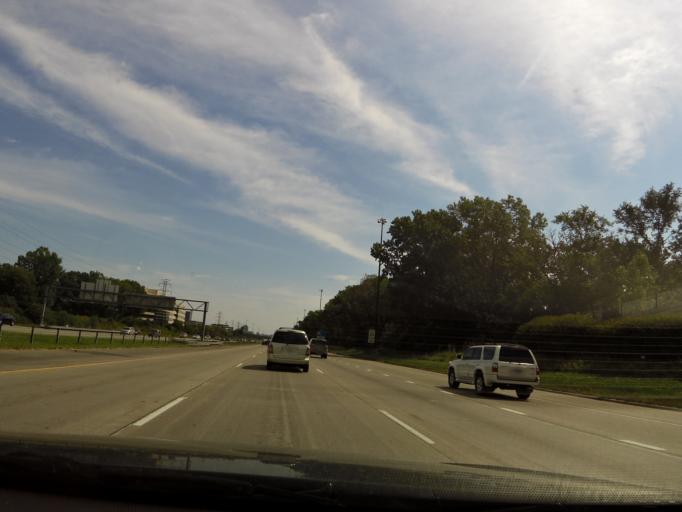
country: US
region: Minnesota
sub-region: Hennepin County
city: Edina
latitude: 44.8602
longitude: -93.3734
